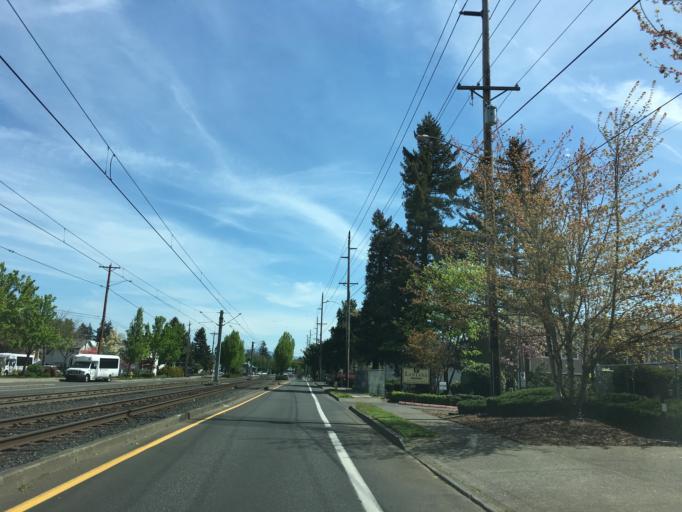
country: US
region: Oregon
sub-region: Multnomah County
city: Fairview
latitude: 45.5220
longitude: -122.4808
